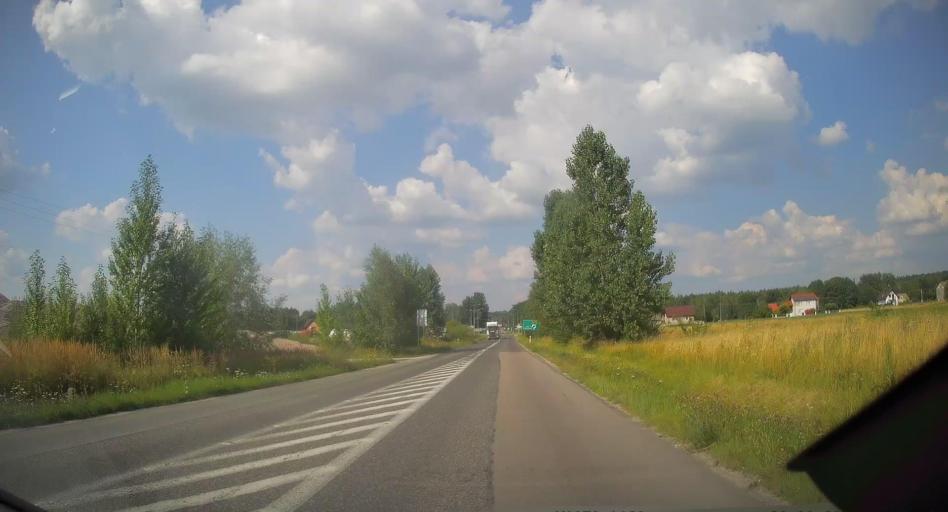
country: PL
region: Swietokrzyskie
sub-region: Powiat kielecki
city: Lopuszno
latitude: 50.9320
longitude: 20.2391
